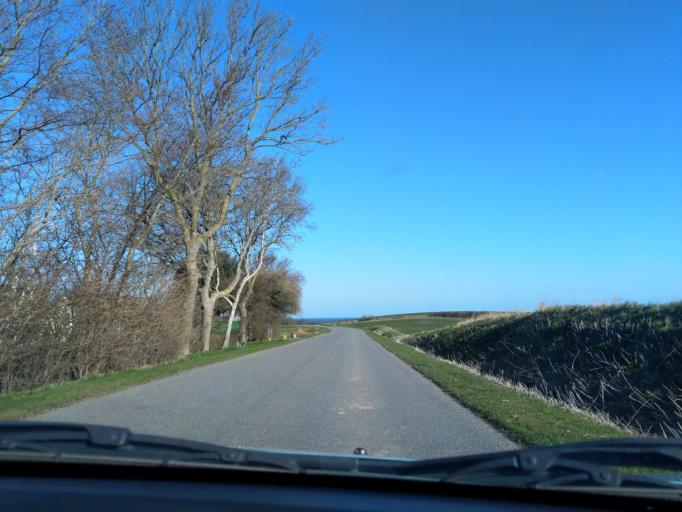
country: DK
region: Zealand
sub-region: Kalundborg Kommune
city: Kalundborg
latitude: 55.7396
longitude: 10.9558
